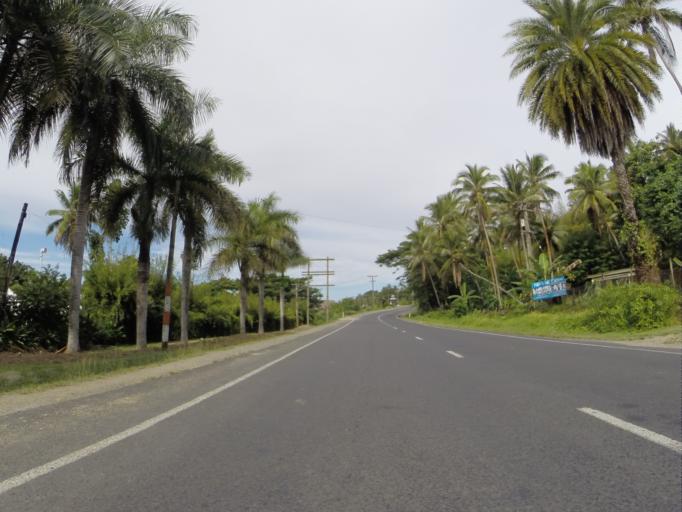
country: FJ
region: Western
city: Nadi
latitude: -18.2013
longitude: 177.6922
